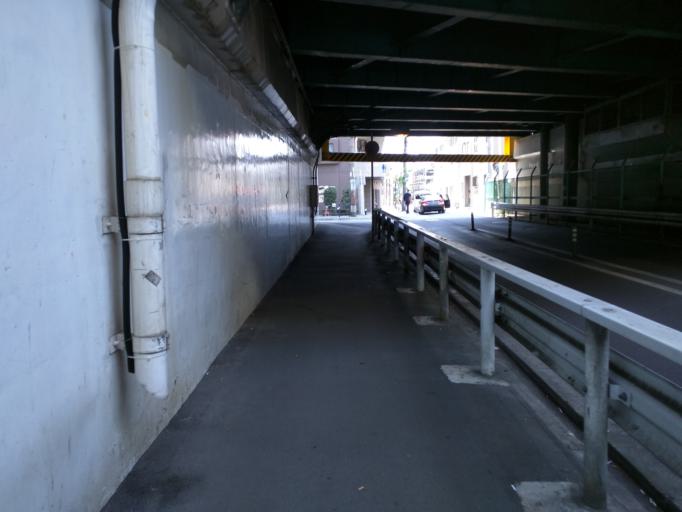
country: JP
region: Osaka
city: Osaka-shi
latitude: 34.6806
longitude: 135.4832
